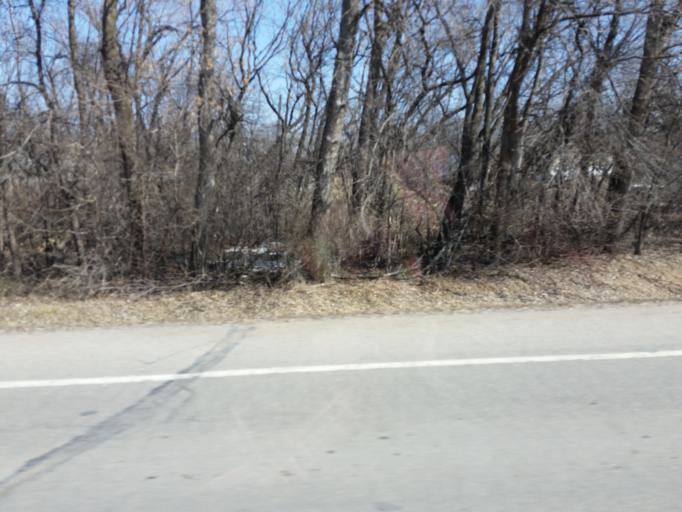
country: US
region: North Dakota
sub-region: Walsh County
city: Grafton
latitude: 48.2858
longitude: -97.3713
